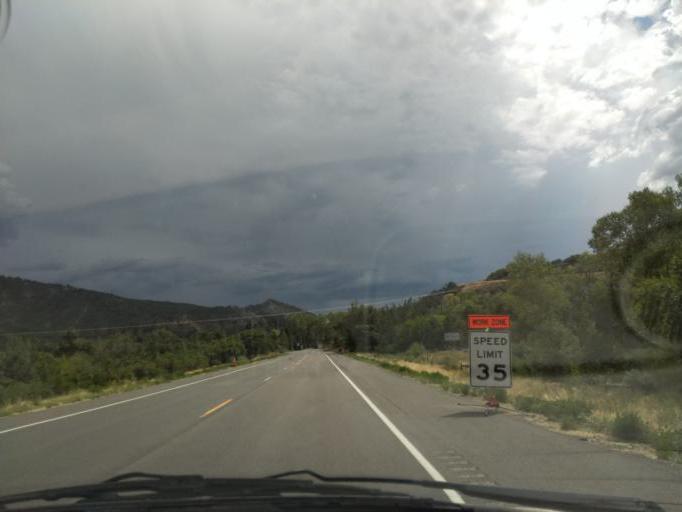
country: US
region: Colorado
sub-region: Delta County
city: Paonia
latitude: 38.9042
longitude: -107.5619
